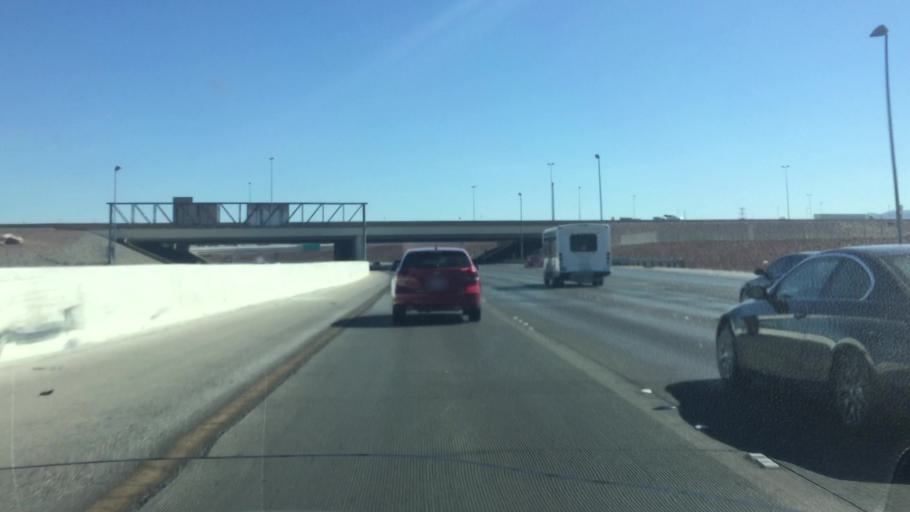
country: US
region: Nevada
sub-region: Clark County
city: Paradise
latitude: 36.0642
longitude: -115.1829
